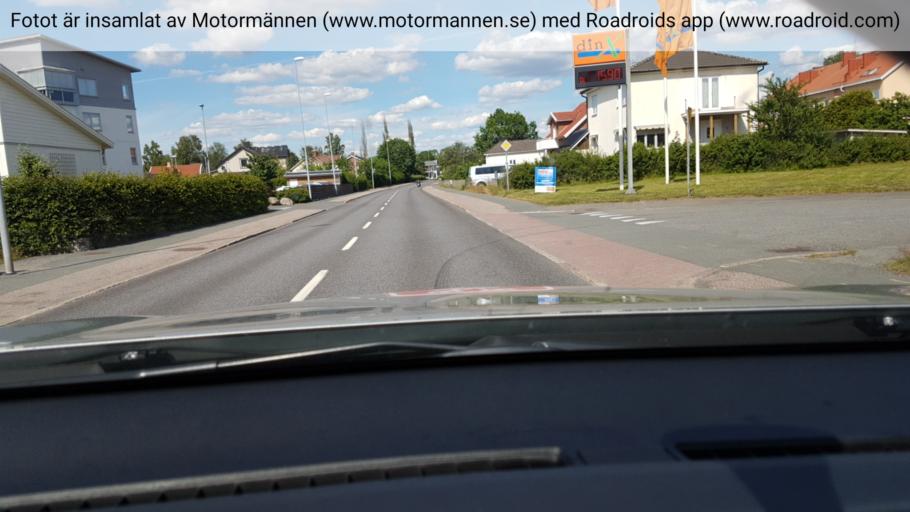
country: SE
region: Joenkoeping
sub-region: Vaggeryds Kommun
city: Vaggeryd
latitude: 57.4969
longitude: 14.1353
